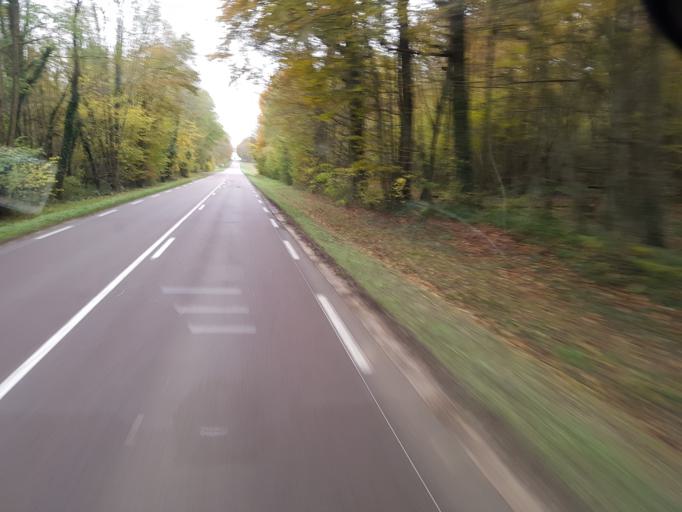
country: FR
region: Champagne-Ardenne
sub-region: Departement de la Marne
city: Esternay
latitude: 48.7940
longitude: 3.6279
